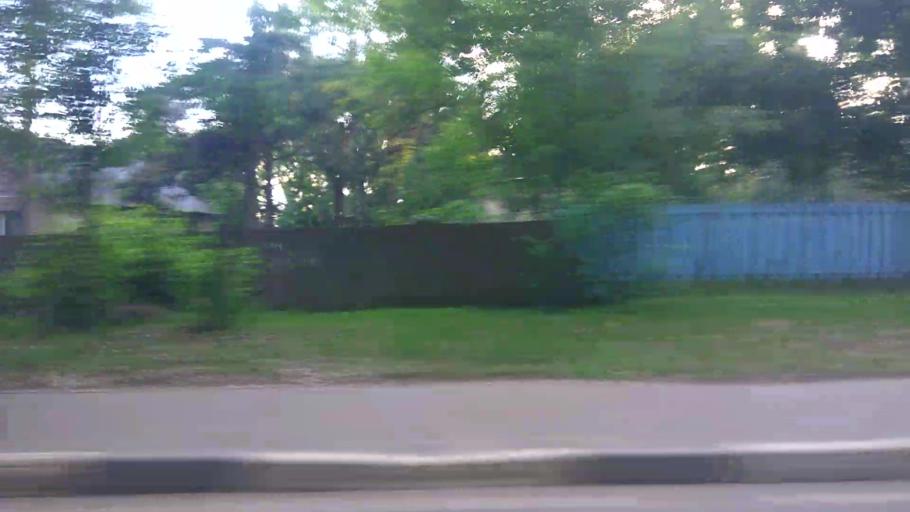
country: RU
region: Moskovskaya
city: Korolev
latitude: 55.9222
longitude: 37.7836
